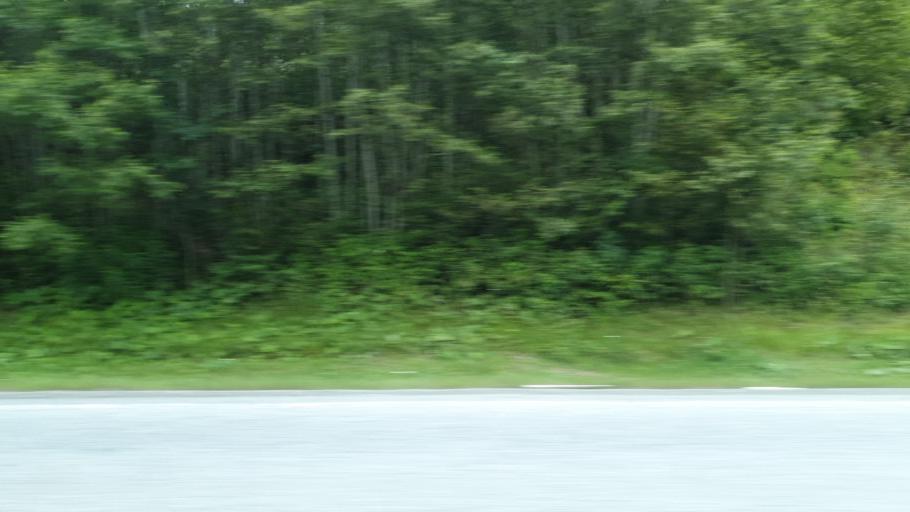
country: NO
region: Sor-Trondelag
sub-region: Midtre Gauldal
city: Storen
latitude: 63.0029
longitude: 10.2380
